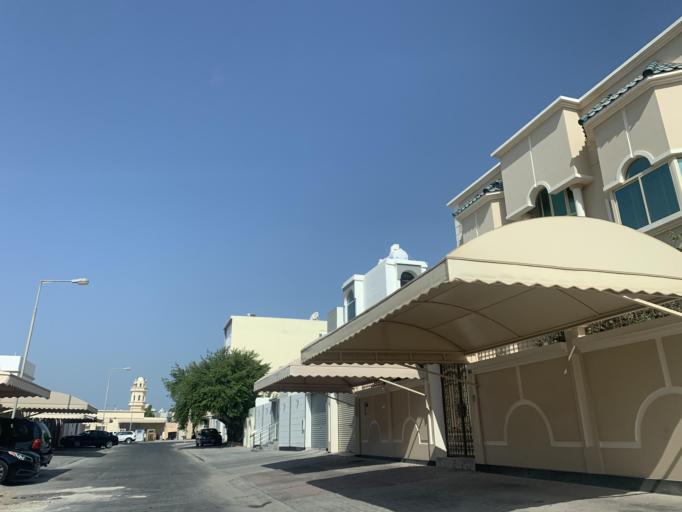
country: BH
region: Central Governorate
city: Madinat Hamad
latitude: 26.1326
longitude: 50.5069
